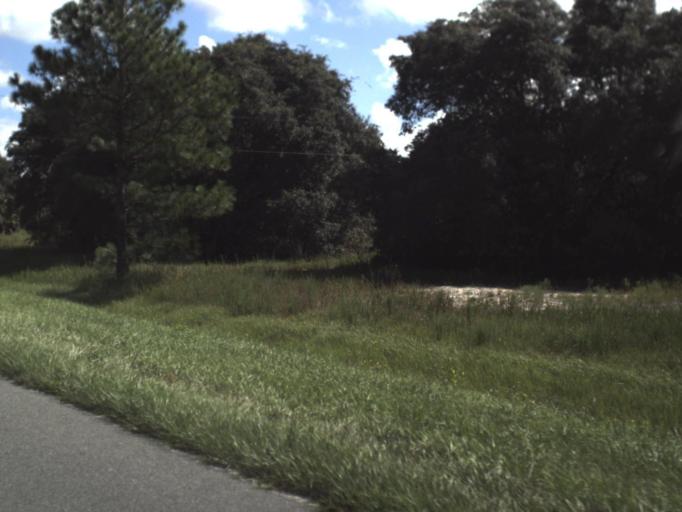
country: US
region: Florida
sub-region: Polk County
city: Loughman
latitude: 28.2122
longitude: -81.5743
